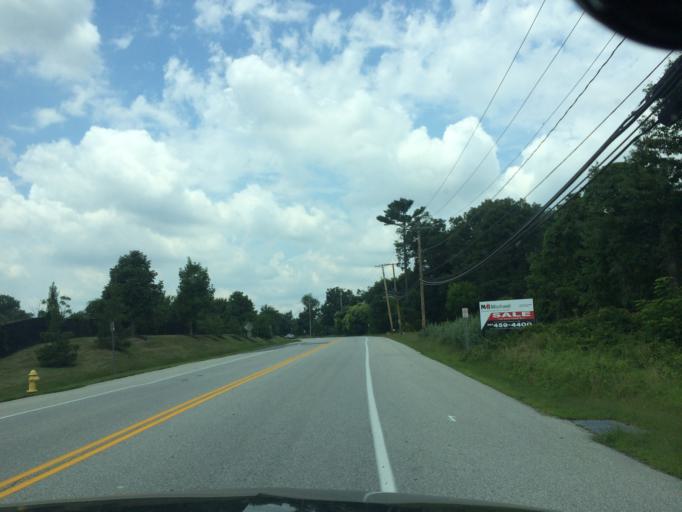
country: US
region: Maryland
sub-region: Howard County
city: Hanover
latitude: 39.1797
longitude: -76.7032
